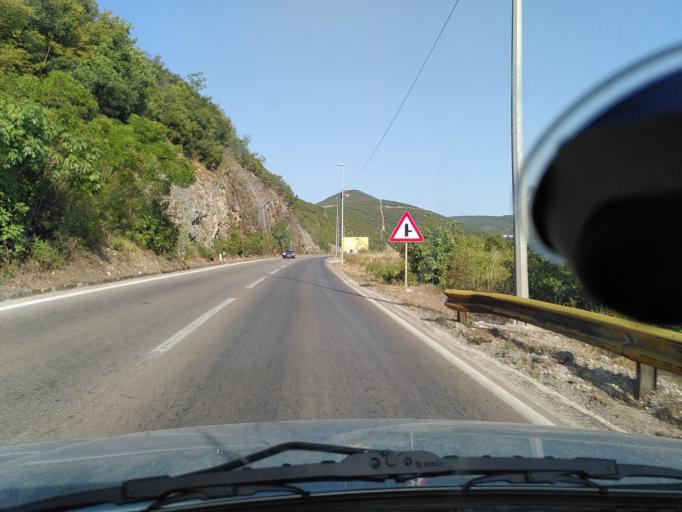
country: ME
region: Ulcinj
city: Ulcinj
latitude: 41.9478
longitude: 19.1998
